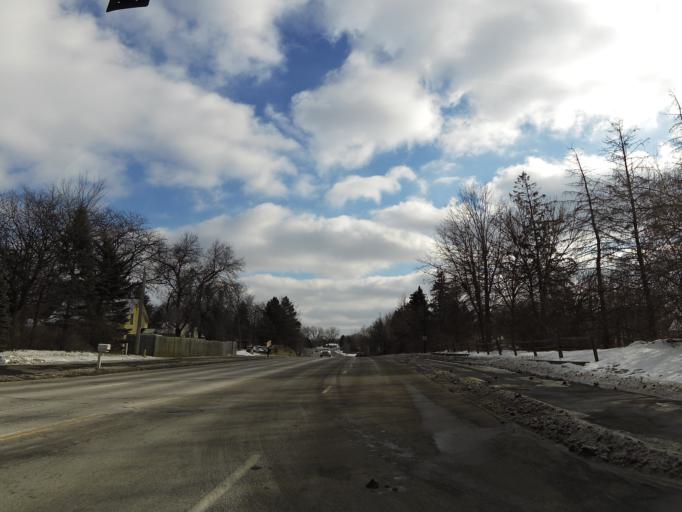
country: US
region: Minnesota
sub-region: Hennepin County
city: Eden Prairie
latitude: 44.8459
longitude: -93.4832
